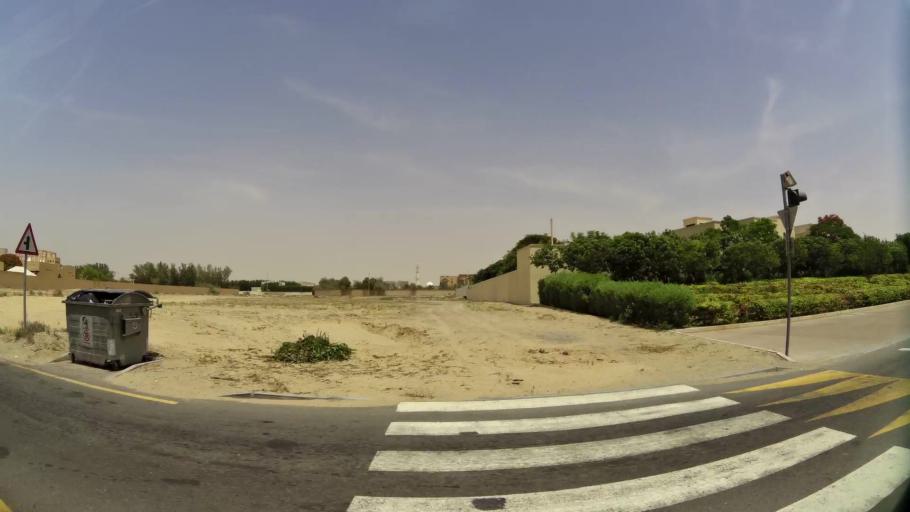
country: AE
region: Ash Shariqah
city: Sharjah
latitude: 25.2412
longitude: 55.4777
